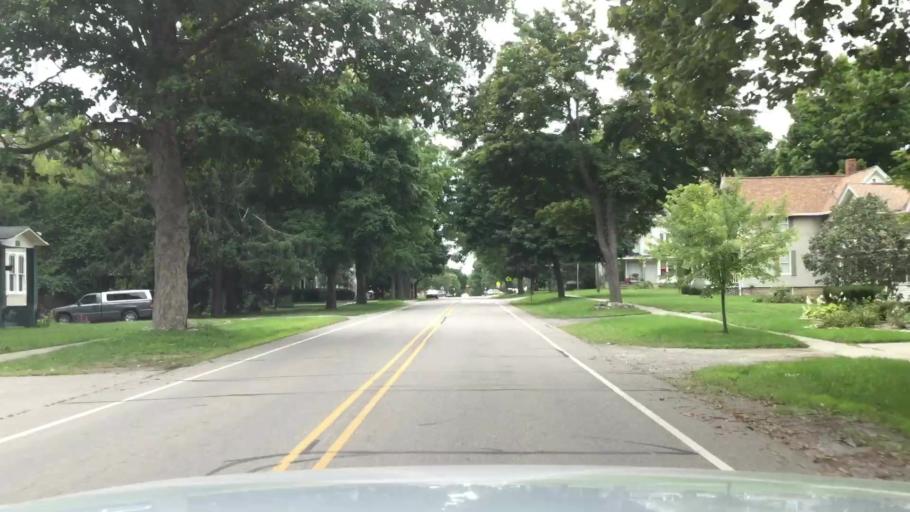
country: US
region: Michigan
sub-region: Shiawassee County
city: Durand
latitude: 42.9393
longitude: -84.0283
